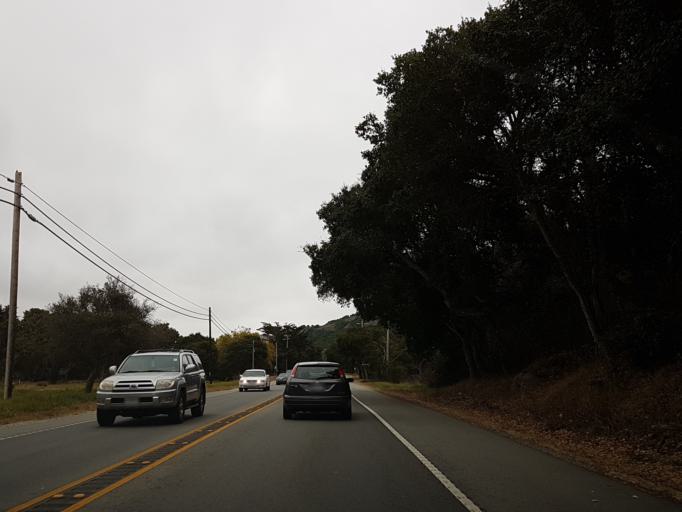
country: US
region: California
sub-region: Monterey County
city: Del Rey Oaks
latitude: 36.5706
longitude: -121.8041
